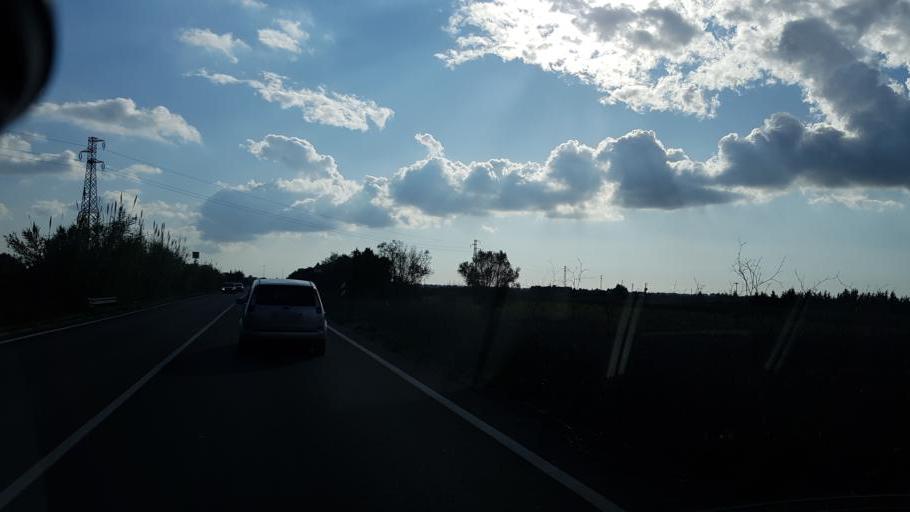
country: IT
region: Apulia
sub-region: Provincia di Lecce
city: Veglie
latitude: 40.3584
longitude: 17.9680
